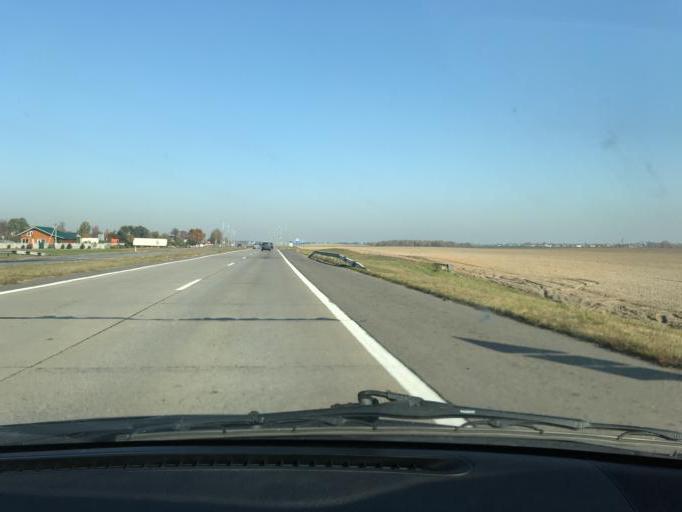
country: BY
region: Minsk
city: Samakhvalavichy
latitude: 53.6738
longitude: 27.4971
